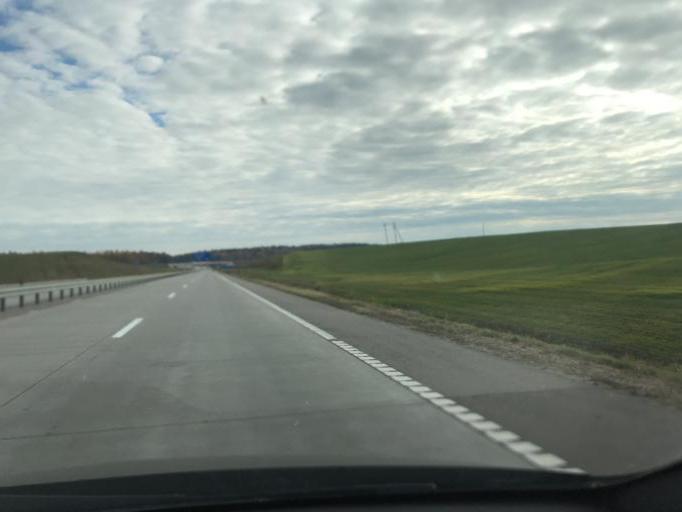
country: BY
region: Minsk
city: Zaslawye
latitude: 54.0698
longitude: 27.2821
